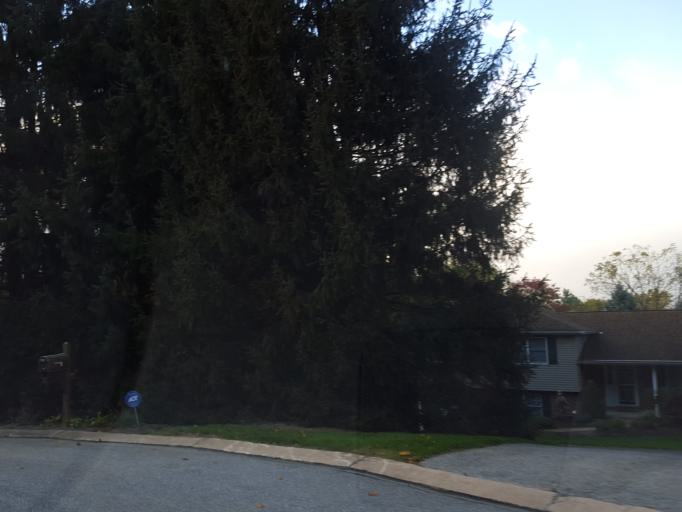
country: US
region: Pennsylvania
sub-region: York County
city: Spry
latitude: 39.9245
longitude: -76.6739
